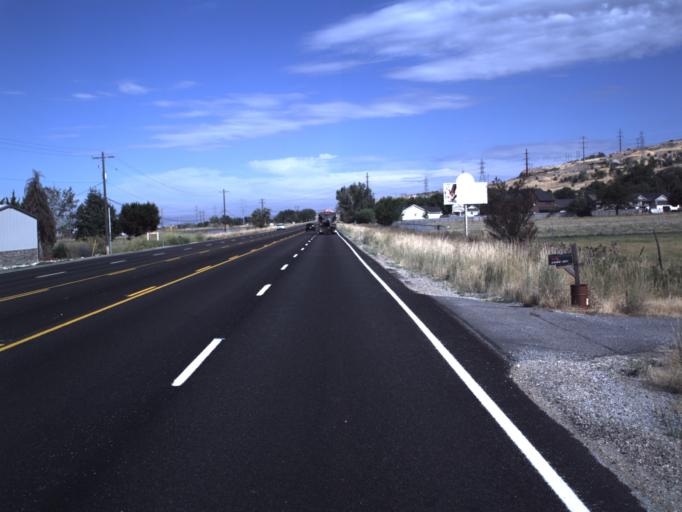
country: US
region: Utah
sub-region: Weber County
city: Pleasant View
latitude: 41.3262
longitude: -112.0204
